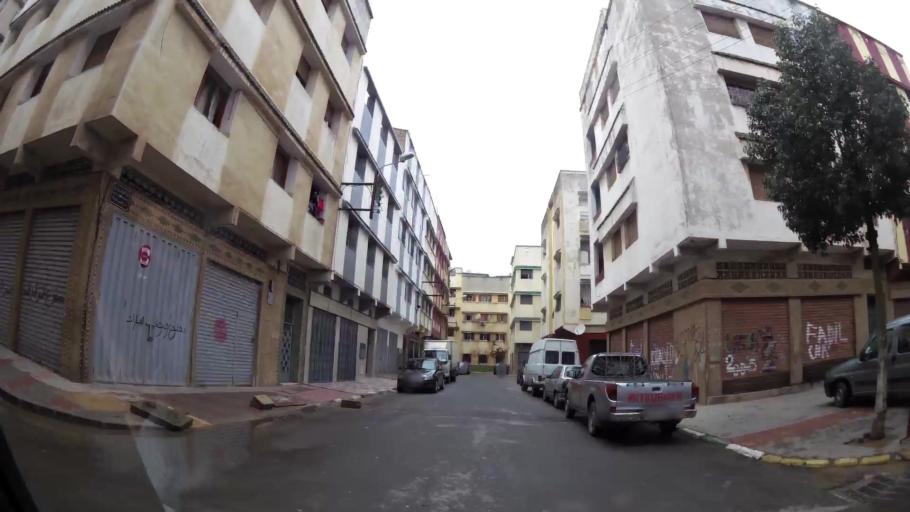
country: MA
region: Grand Casablanca
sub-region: Casablanca
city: Casablanca
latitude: 33.5377
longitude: -7.5734
